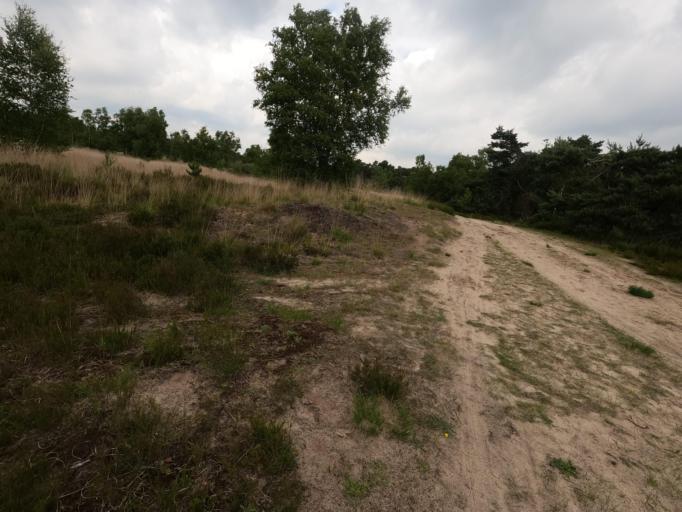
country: BE
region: Flanders
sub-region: Provincie Antwerpen
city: Kalmthout
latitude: 51.3543
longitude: 4.4981
